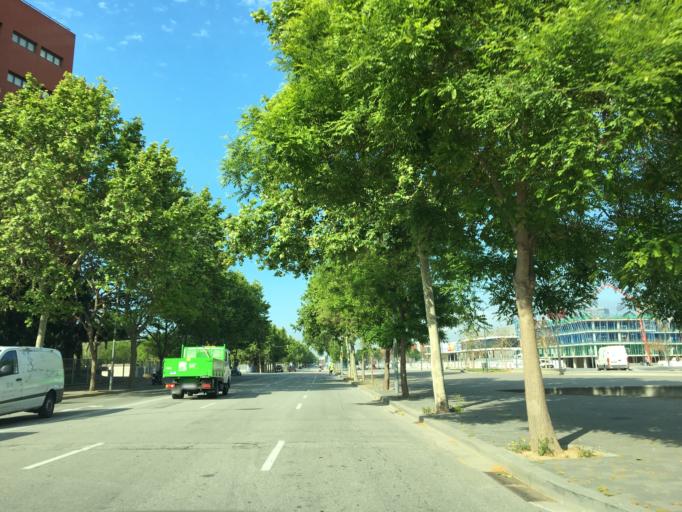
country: ES
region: Catalonia
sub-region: Provincia de Barcelona
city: Sants-Montjuic
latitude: 41.3563
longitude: 2.1414
